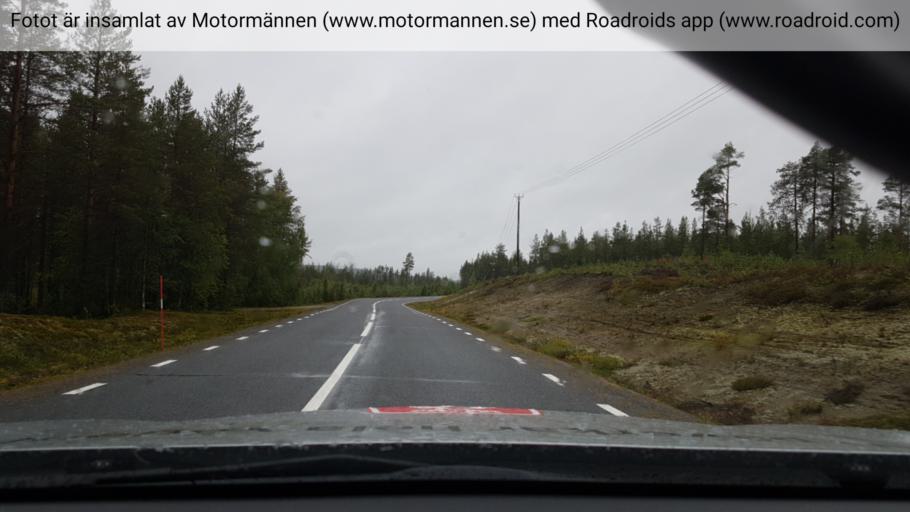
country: SE
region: Vaesterbotten
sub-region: Asele Kommun
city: Asele
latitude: 64.0668
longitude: 17.6147
